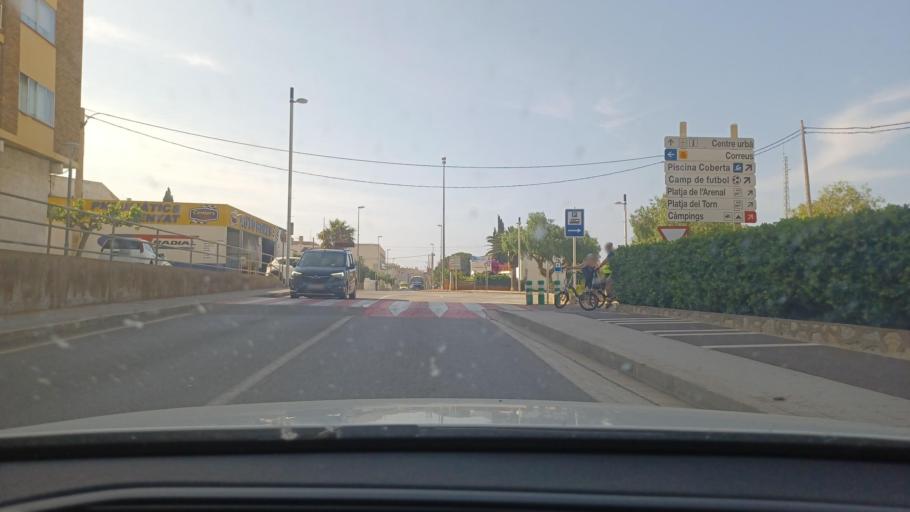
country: ES
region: Catalonia
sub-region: Provincia de Tarragona
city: Colldejou
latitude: 40.9952
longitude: 0.9200
